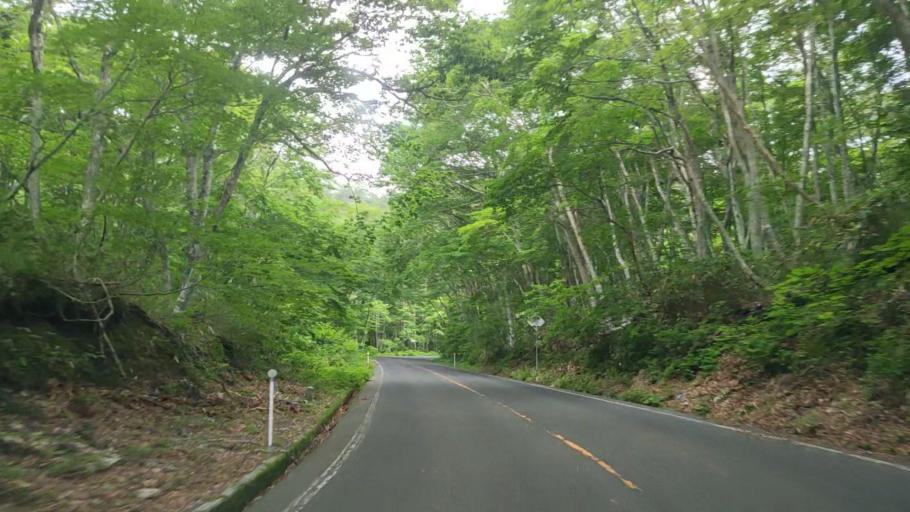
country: JP
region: Tottori
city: Yonago
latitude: 35.3444
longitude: 133.5545
